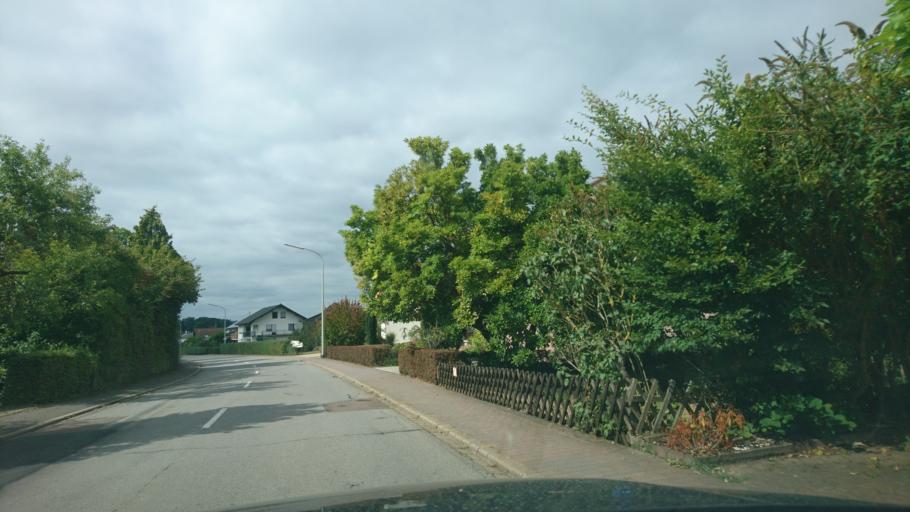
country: DE
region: Rheinland-Pfalz
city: Wiltingen
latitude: 49.6539
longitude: 6.5971
